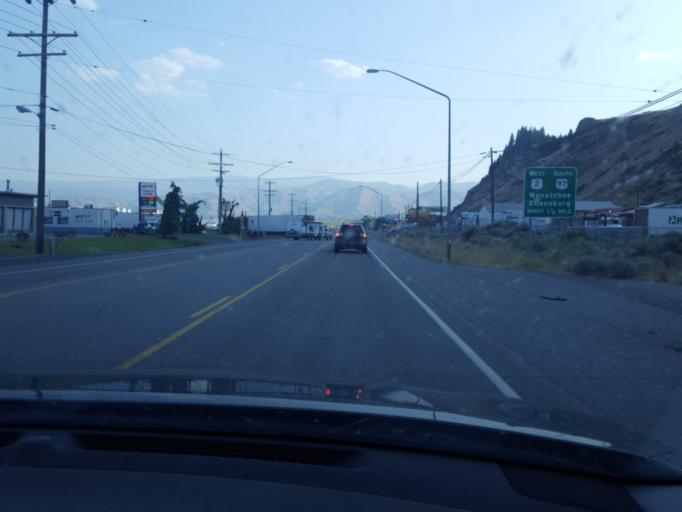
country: US
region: Washington
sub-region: Chelan County
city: Sunnyslope
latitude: 47.4850
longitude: -120.3180
